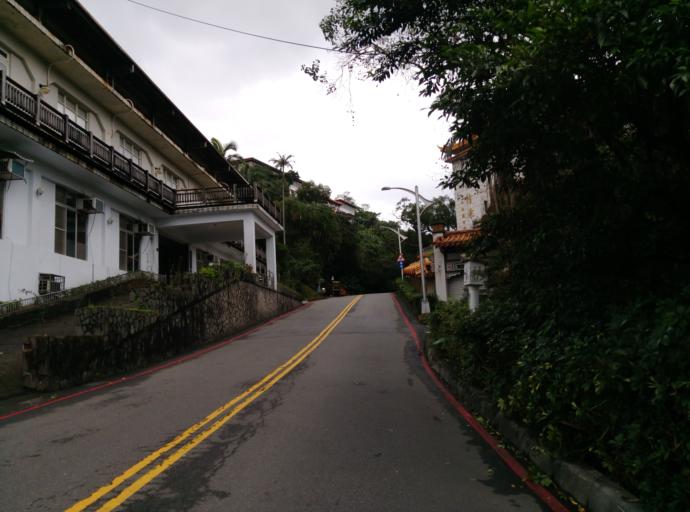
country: TW
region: Taiwan
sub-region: Keelung
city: Keelung
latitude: 25.1321
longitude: 121.7495
